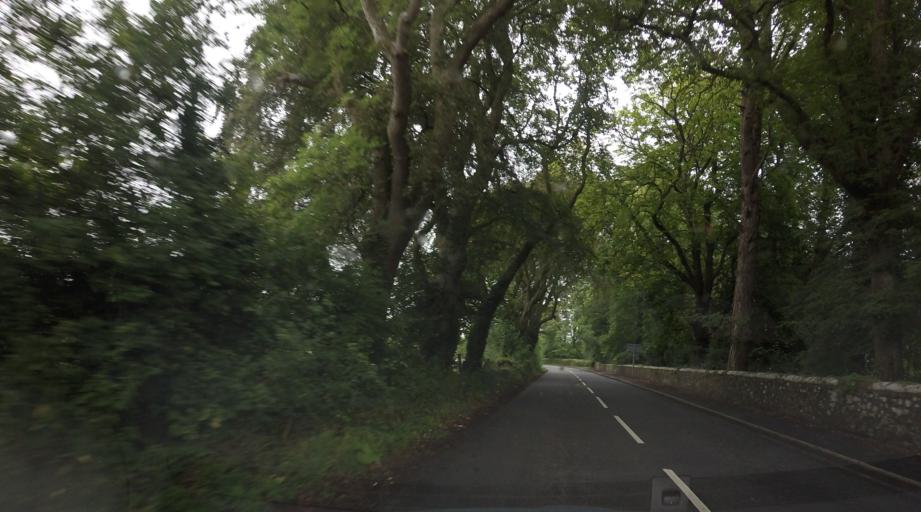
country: GB
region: Scotland
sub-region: South Ayrshire
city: Ayr
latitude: 55.4244
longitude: -4.6401
